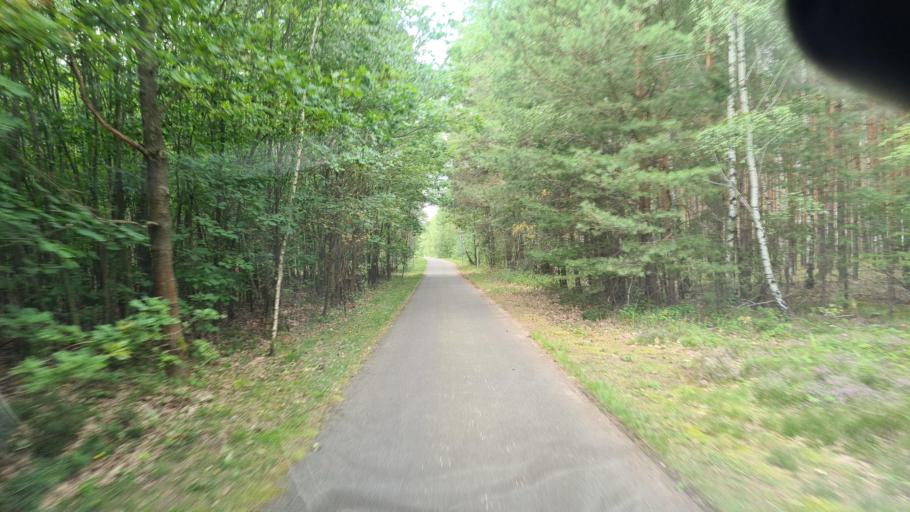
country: DE
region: Brandenburg
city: Sallgast
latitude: 51.5882
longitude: 13.8698
